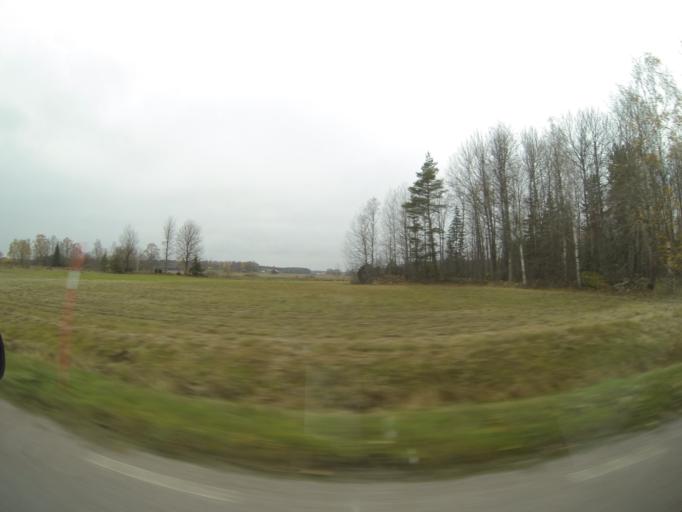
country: SE
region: Vaestmanland
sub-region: Kopings Kommun
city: Koping
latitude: 59.5802
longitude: 16.0836
